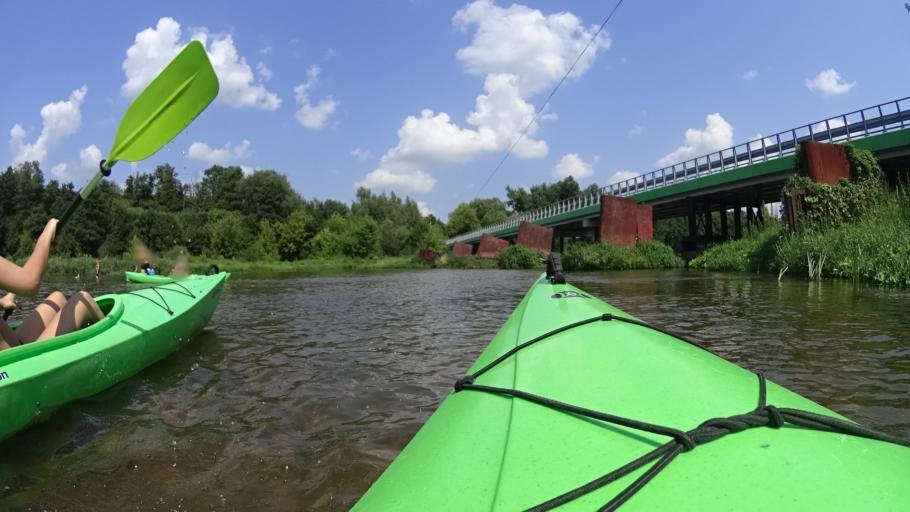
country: PL
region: Masovian Voivodeship
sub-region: Powiat grojecki
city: Mogielnica
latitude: 51.6279
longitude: 20.6955
